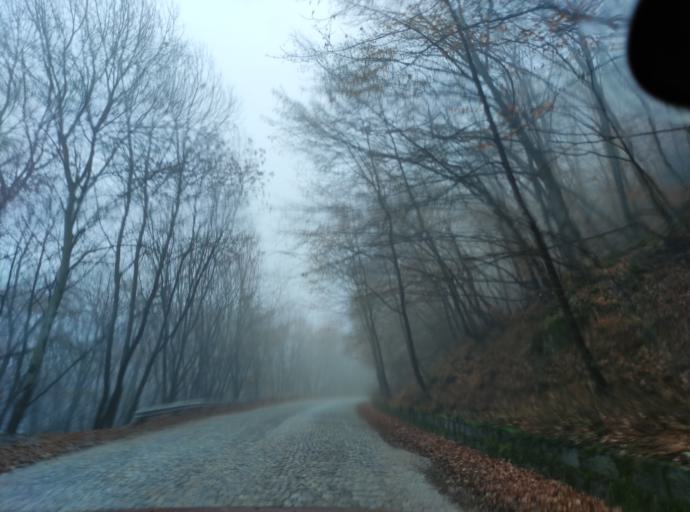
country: BG
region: Sofia-Capital
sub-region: Stolichna Obshtina
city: Sofia
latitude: 42.6236
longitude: 23.2963
